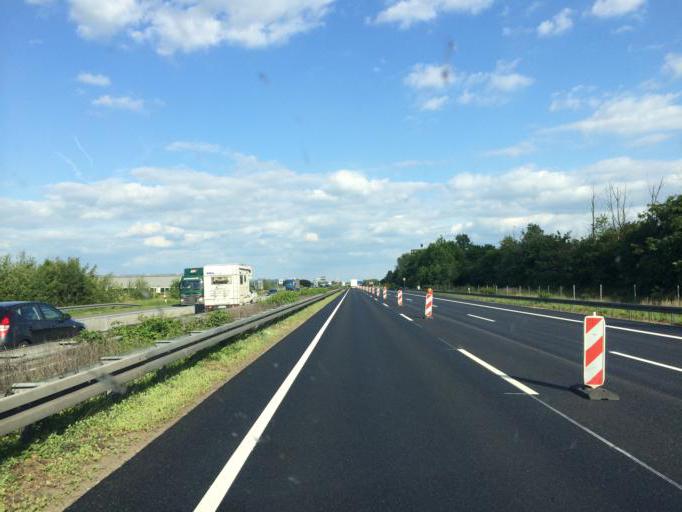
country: DE
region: Lower Saxony
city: Klein Schwulper
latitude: 52.3231
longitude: 10.4809
